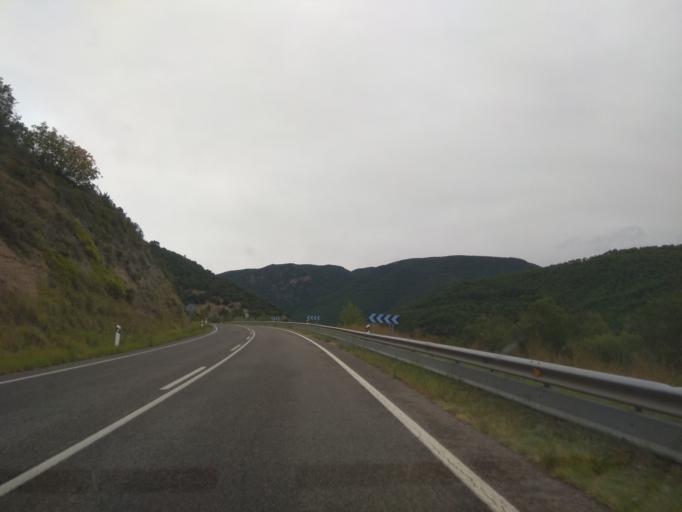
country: ES
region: Catalonia
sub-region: Provincia de Lleida
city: Alas i Cerc
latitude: 42.3593
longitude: 1.5607
